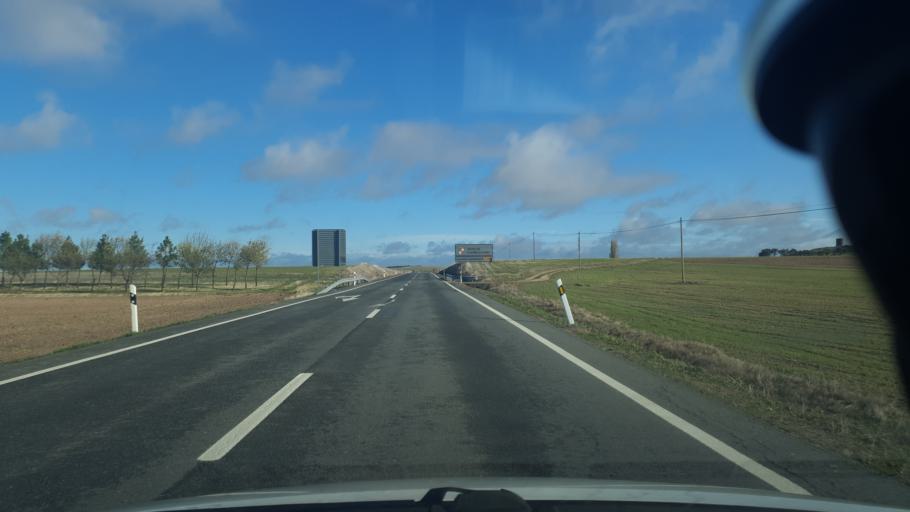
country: ES
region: Castille and Leon
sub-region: Provincia de Segovia
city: Codorniz
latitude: 41.0532
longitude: -4.6219
